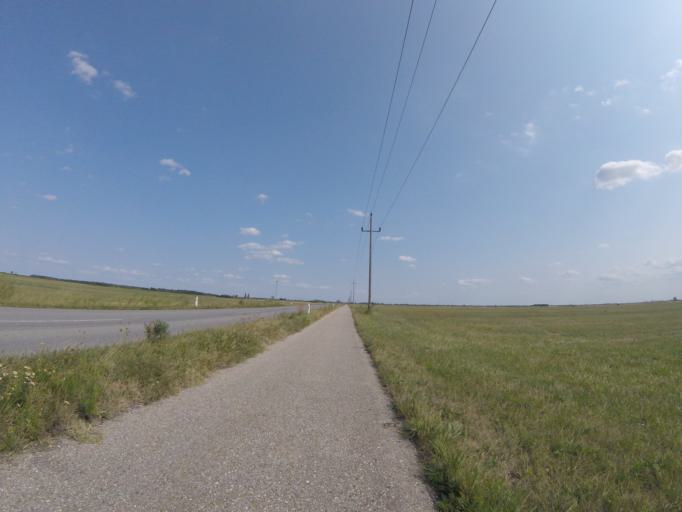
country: AT
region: Burgenland
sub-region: Politischer Bezirk Neusiedl am See
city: Apetlon
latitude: 47.7292
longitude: 16.8512
